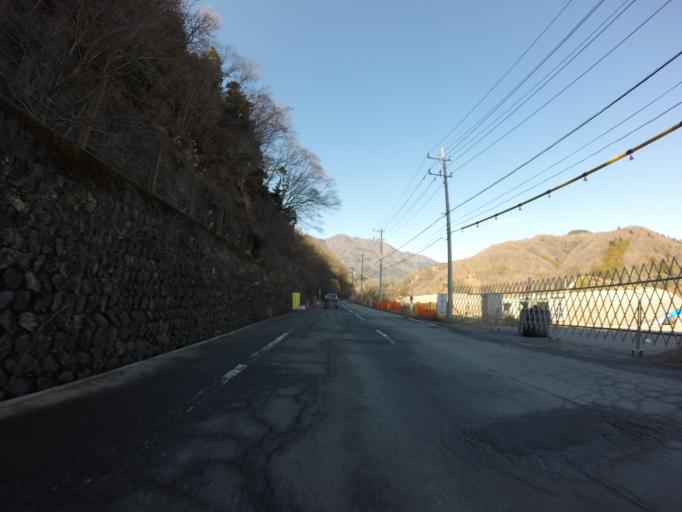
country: JP
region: Yamanashi
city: Ryuo
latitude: 35.4285
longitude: 138.4263
